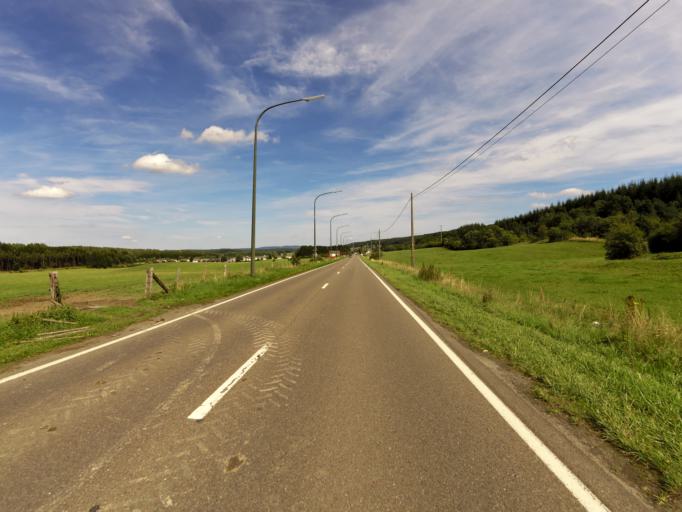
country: BE
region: Wallonia
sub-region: Province du Luxembourg
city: Marche-en-Famenne
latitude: 50.2398
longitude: 5.3737
